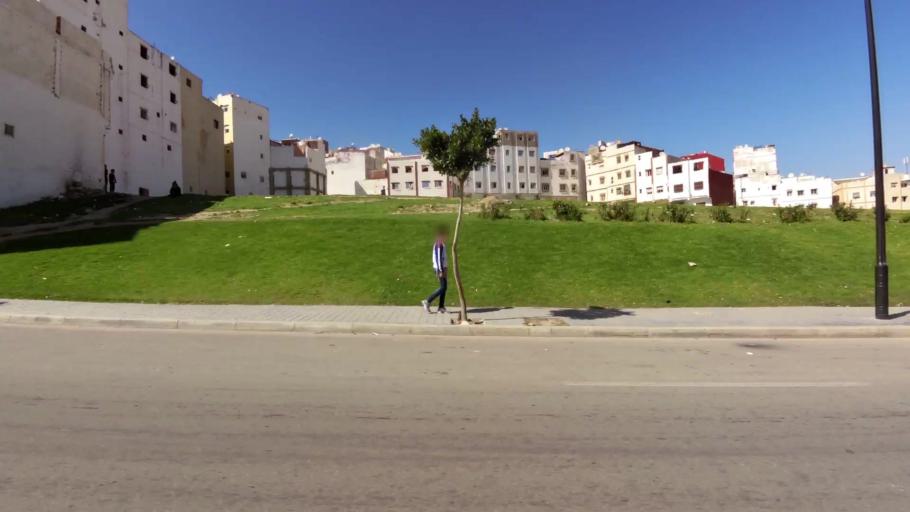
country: MA
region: Tanger-Tetouan
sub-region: Tanger-Assilah
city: Tangier
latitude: 35.7419
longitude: -5.8090
